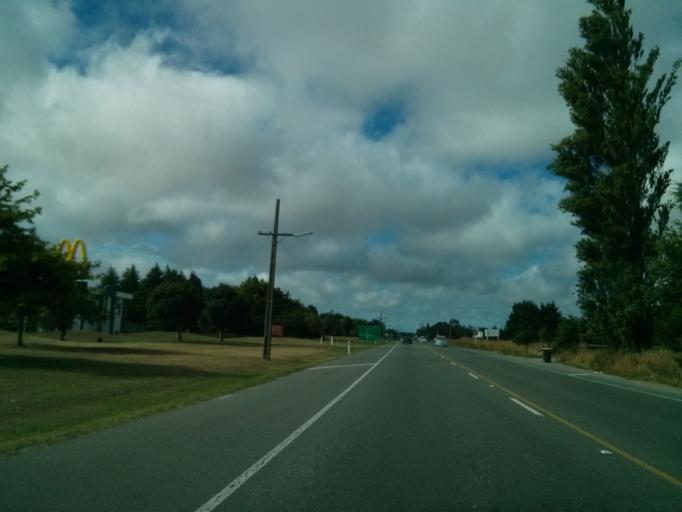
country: NZ
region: Canterbury
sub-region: Selwyn District
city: Prebbleton
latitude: -43.4962
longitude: 172.5481
